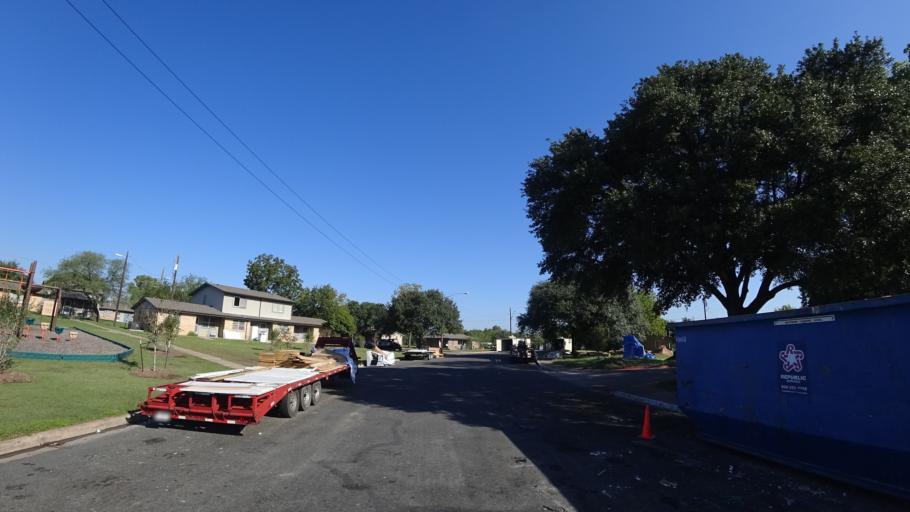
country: US
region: Texas
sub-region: Travis County
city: Austin
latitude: 30.3502
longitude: -97.7029
